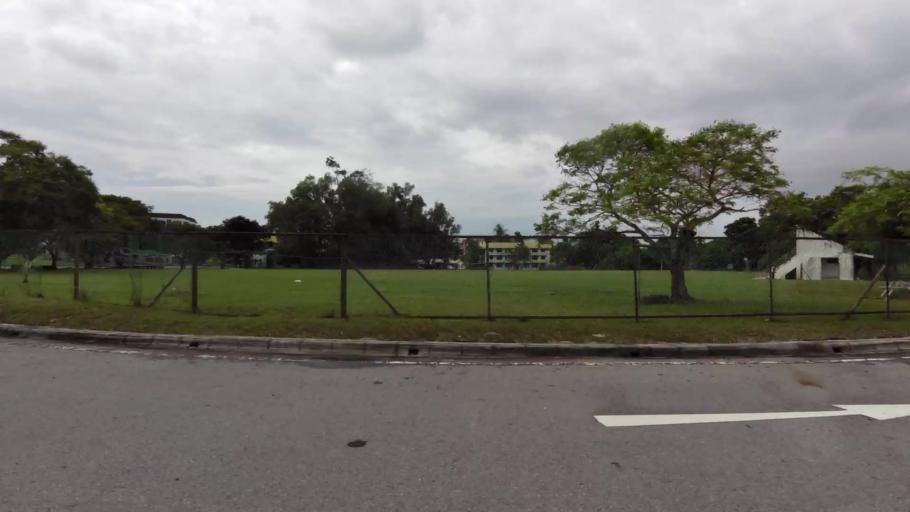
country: BN
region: Brunei and Muara
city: Bandar Seri Begawan
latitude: 4.9051
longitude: 114.9354
